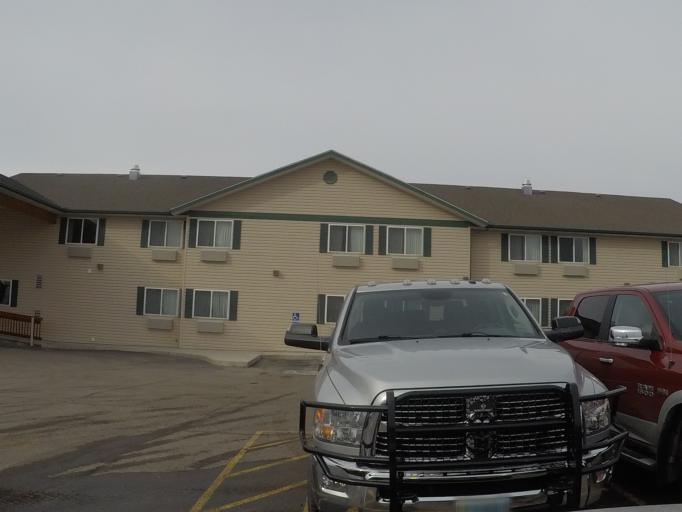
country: US
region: Montana
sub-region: Meagher County
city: White Sulphur Springs
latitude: 46.5417
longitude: -110.9059
